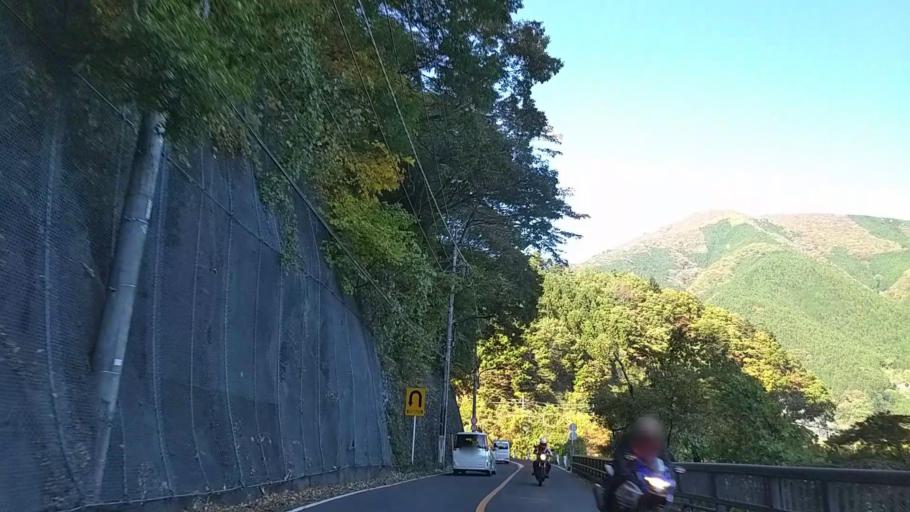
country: JP
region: Yamanashi
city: Uenohara
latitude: 35.7848
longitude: 139.0443
